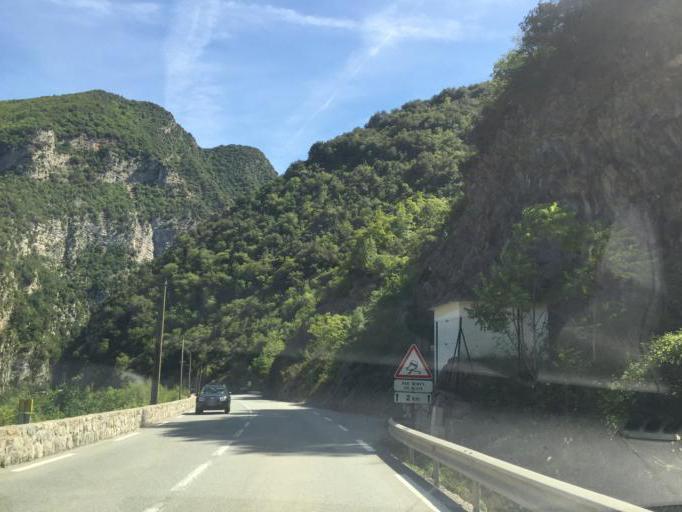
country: FR
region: Provence-Alpes-Cote d'Azur
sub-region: Departement des Alpes-Maritimes
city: Levens
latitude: 43.9223
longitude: 7.1859
